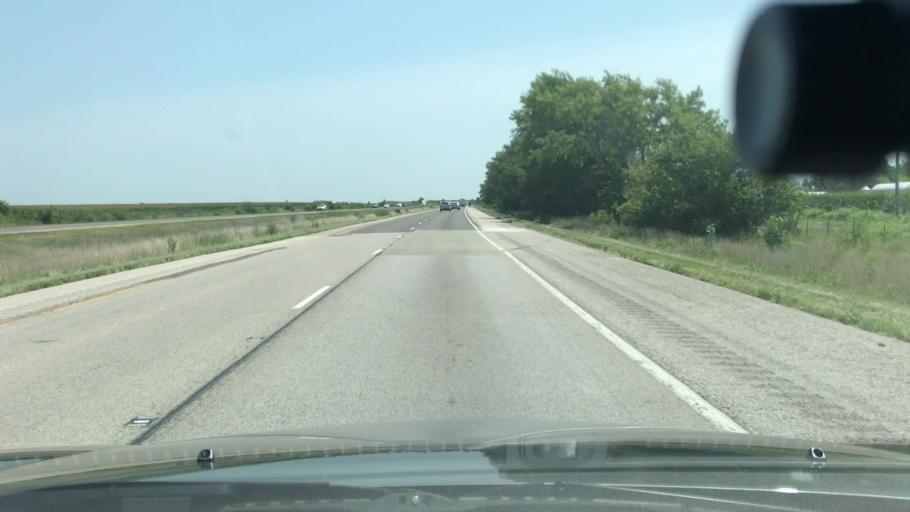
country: US
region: Illinois
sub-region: Washington County
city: Nashville
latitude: 38.3911
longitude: -89.2921
